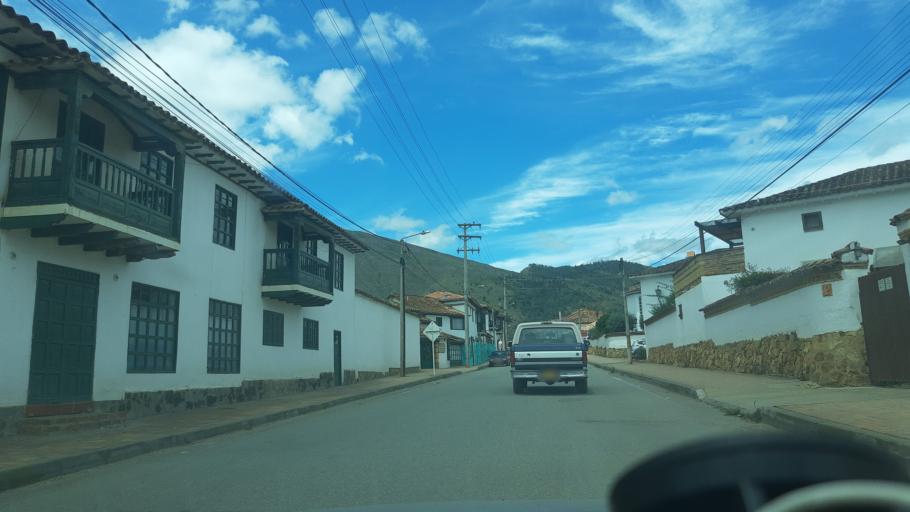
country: CO
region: Boyaca
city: Villa de Leiva
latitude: 5.6335
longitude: -73.5280
